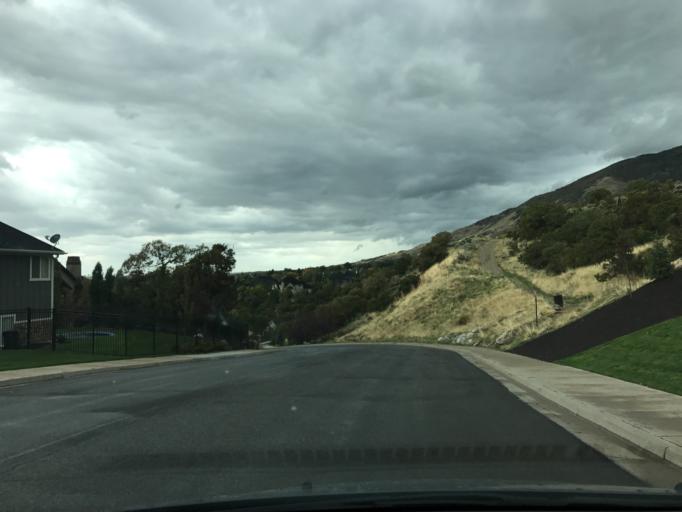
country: US
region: Utah
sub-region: Davis County
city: Fruit Heights
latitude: 41.0155
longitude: -111.8988
